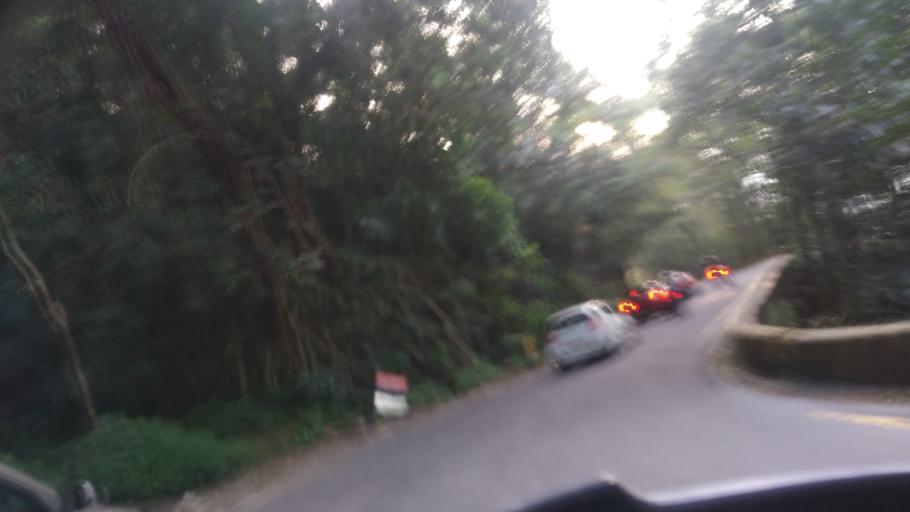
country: IN
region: Kerala
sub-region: Wayanad
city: Kalpetta
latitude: 11.5023
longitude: 76.0270
